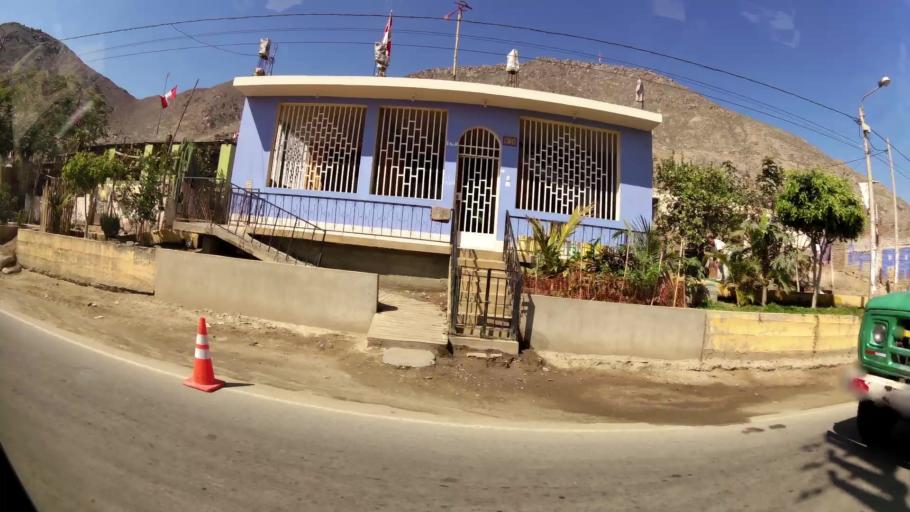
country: PE
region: Ica
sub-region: Provincia de Ica
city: San Juan Bautista
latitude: -13.9587
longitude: -75.6914
